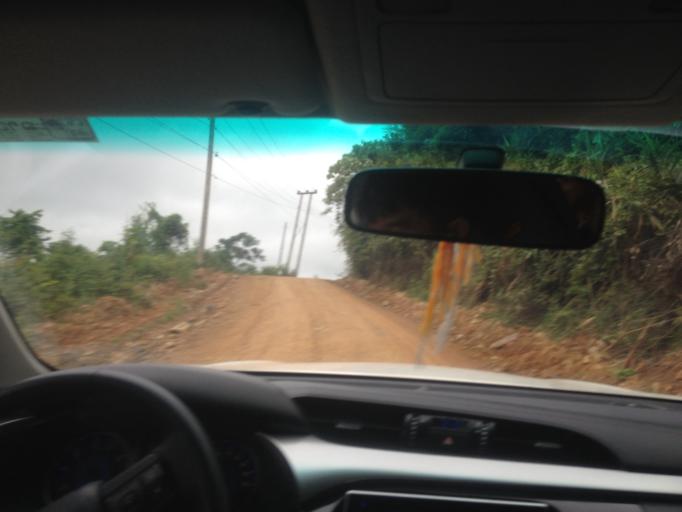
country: TH
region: Nan
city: Chaloem Phra Kiat
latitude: 19.9725
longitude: 101.1364
